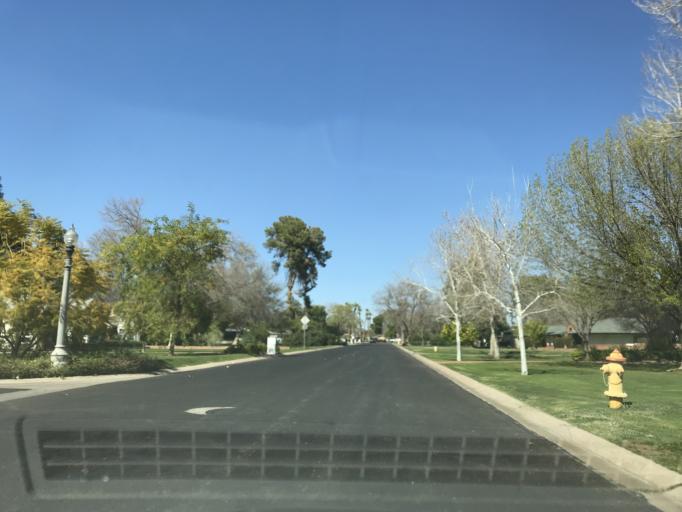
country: US
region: Arizona
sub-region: Maricopa County
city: Phoenix
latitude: 33.5218
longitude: -112.0760
